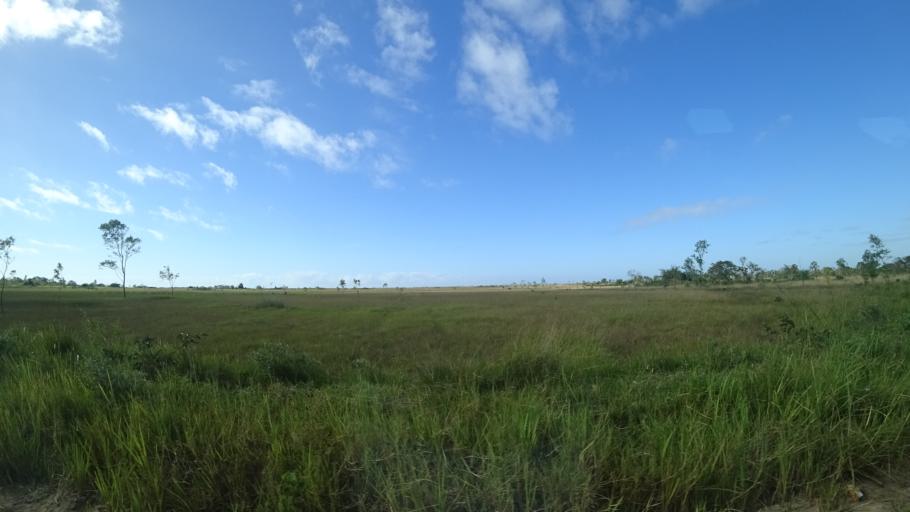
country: MZ
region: Sofala
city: Beira
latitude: -19.7204
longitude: 35.0001
